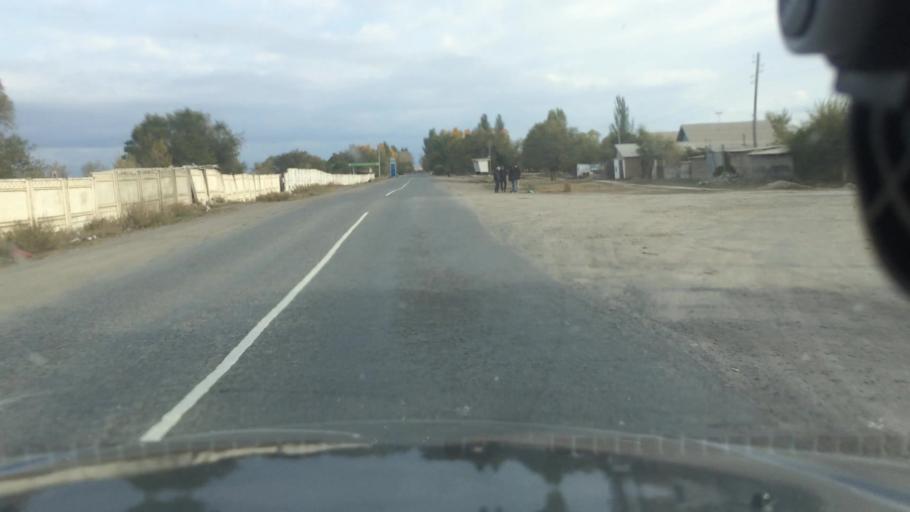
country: KG
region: Ysyk-Koel
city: Karakol
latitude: 42.5375
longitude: 78.3823
